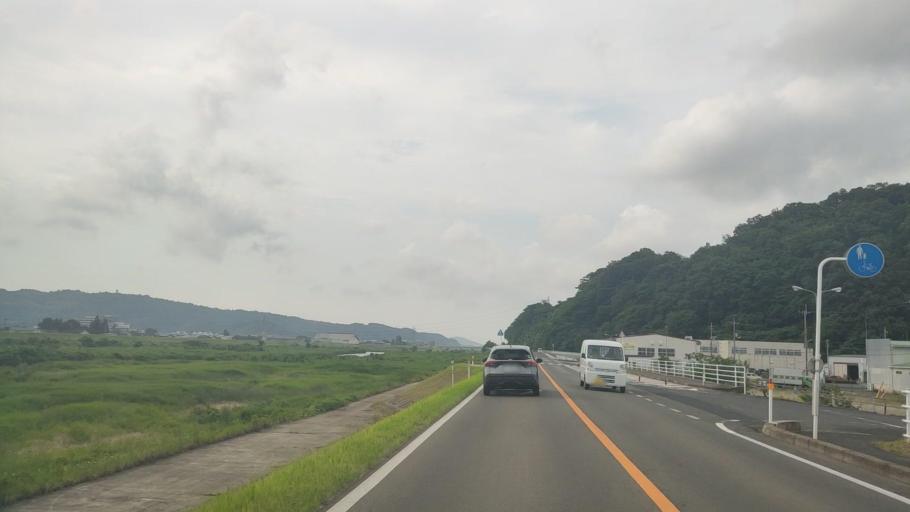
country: JP
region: Tottori
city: Kurayoshi
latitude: 35.4281
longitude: 133.8501
